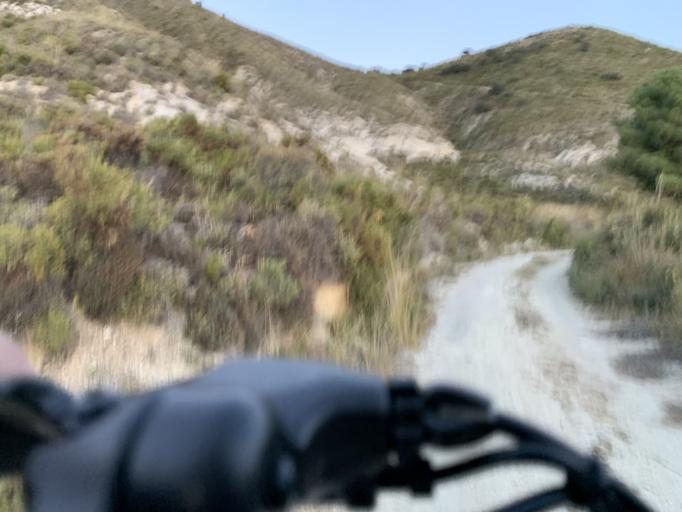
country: ES
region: Andalusia
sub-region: Provincia de Granada
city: Beas de Granada
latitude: 37.2264
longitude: -3.4600
